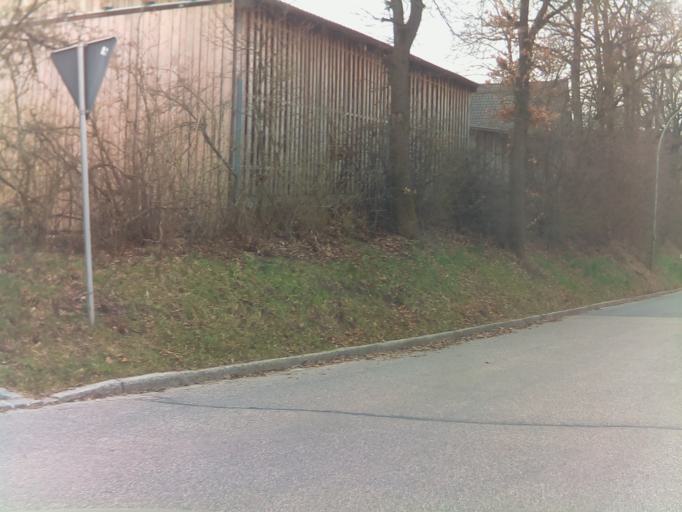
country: DE
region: Bavaria
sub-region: Upper Palatinate
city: Schmidgaden
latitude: 49.4358
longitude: 12.0559
